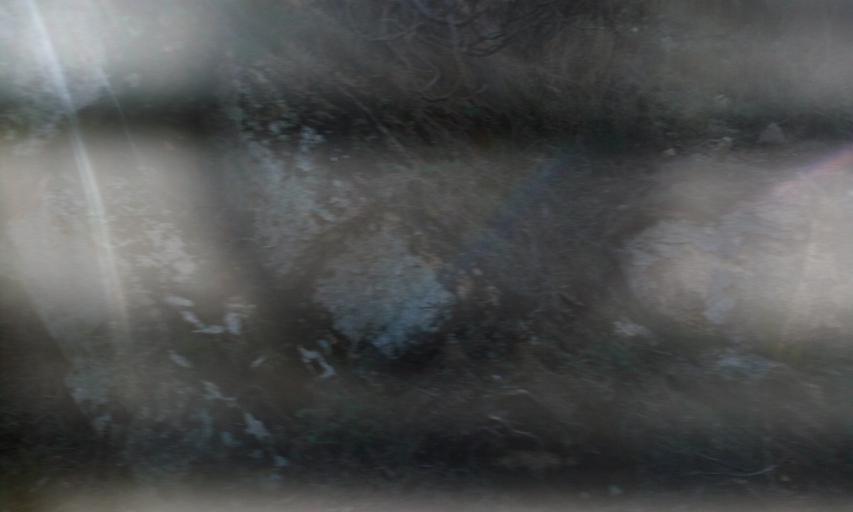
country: PT
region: Guarda
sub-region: Manteigas
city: Manteigas
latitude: 40.4844
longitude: -7.5169
